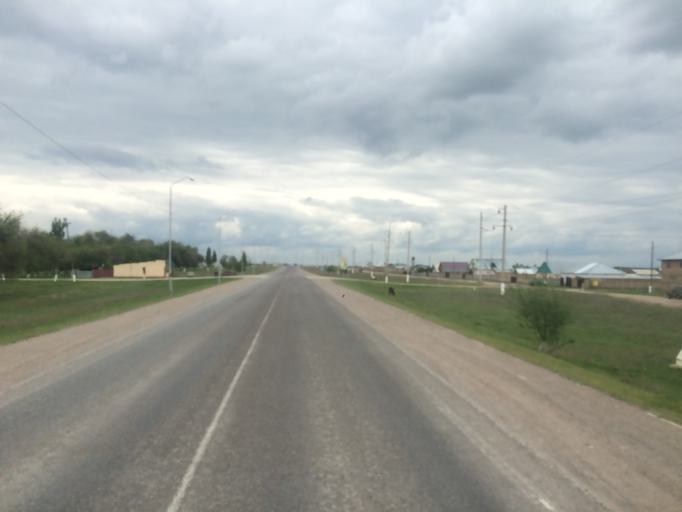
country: KG
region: Chuy
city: Sokuluk
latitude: 43.2487
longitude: 74.2934
